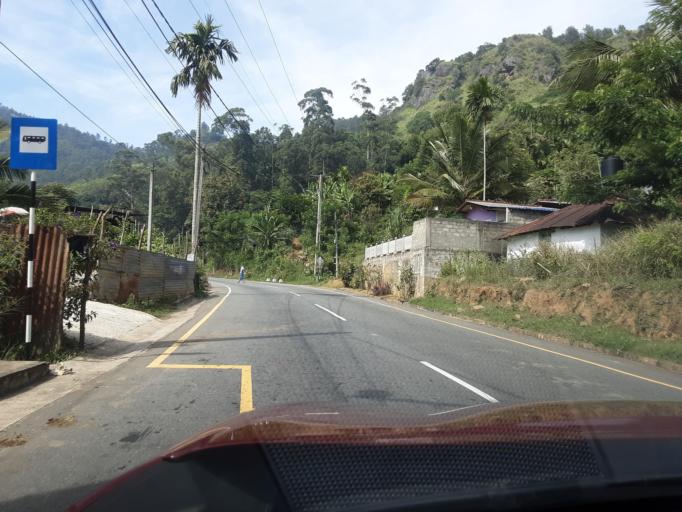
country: LK
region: Uva
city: Badulla
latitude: 6.9714
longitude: 81.0862
